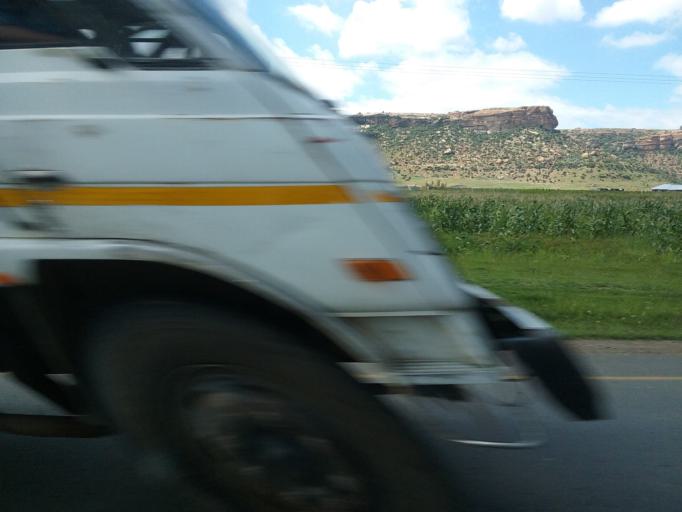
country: LS
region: Maseru
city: Maseru
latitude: -29.2645
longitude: 27.6014
